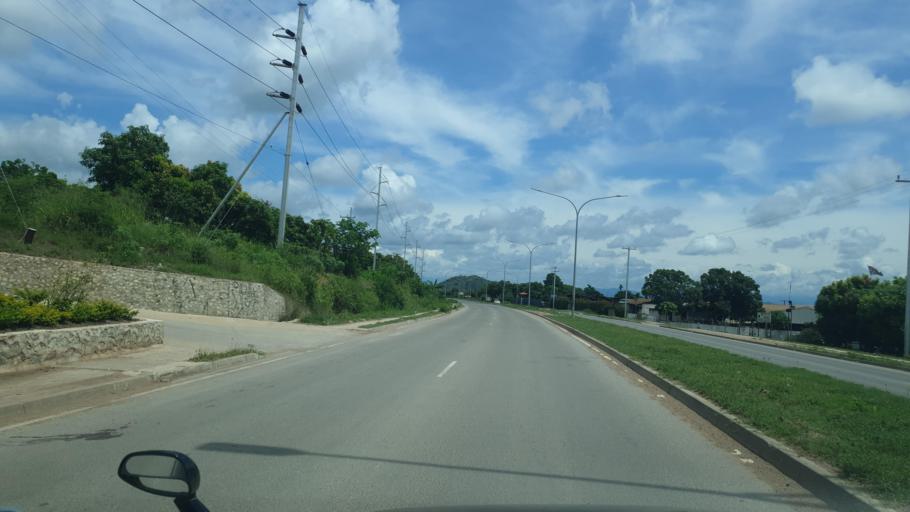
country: PG
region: National Capital
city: Port Moresby
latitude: -9.3866
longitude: 147.1546
